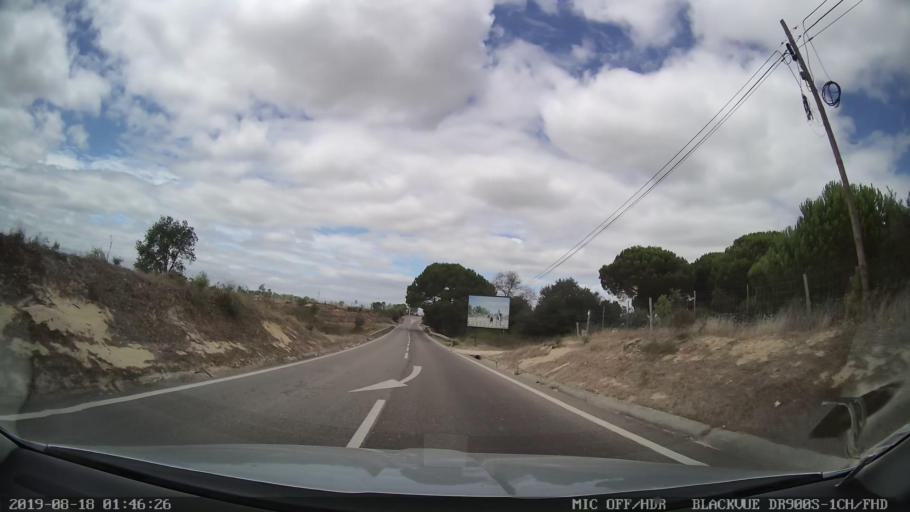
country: PT
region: Santarem
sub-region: Benavente
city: Benavente
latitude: 38.9341
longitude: -8.7814
